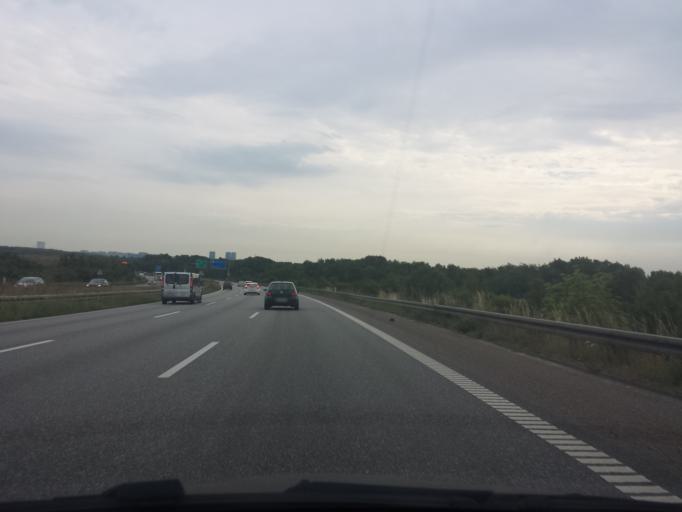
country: DK
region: Capital Region
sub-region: Hvidovre Kommune
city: Hvidovre
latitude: 55.6140
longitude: 12.5177
